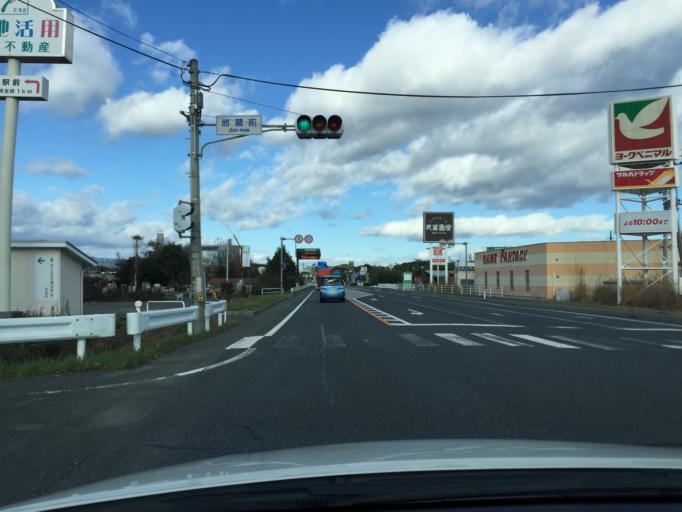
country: JP
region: Fukushima
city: Namie
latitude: 37.4917
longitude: 141.0035
